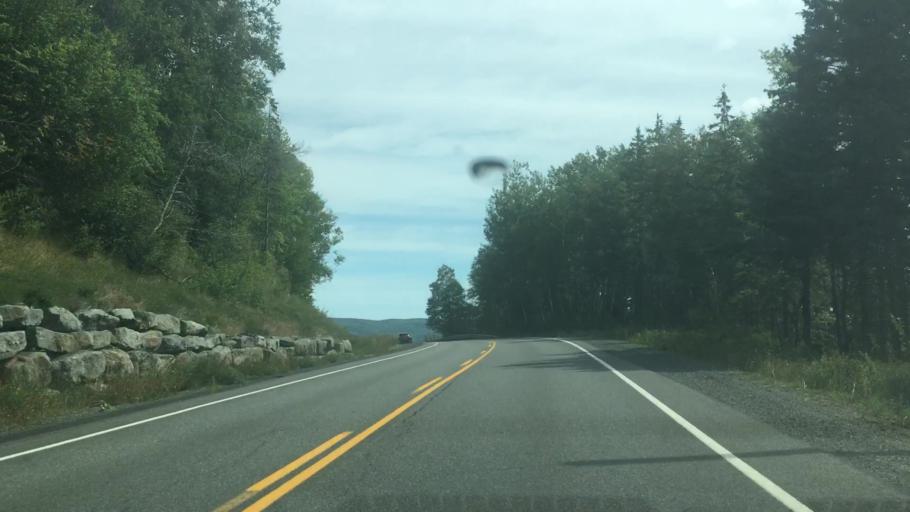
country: CA
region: Nova Scotia
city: Sydney Mines
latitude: 46.2655
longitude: -60.6138
